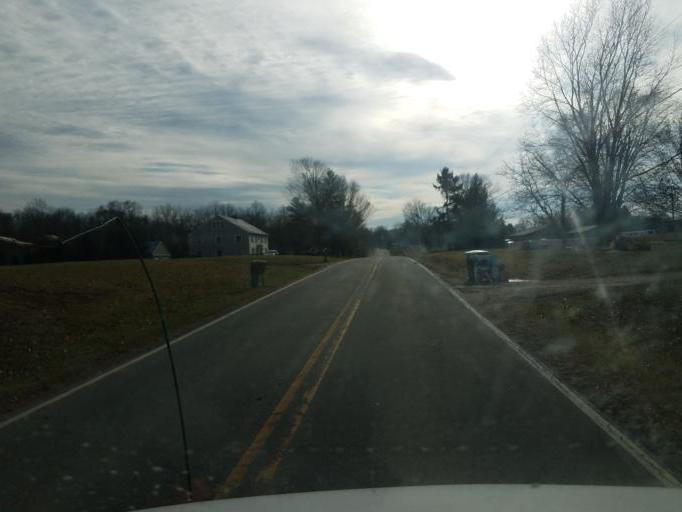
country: US
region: Ohio
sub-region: Delaware County
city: Delaware
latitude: 40.2939
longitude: -82.9653
